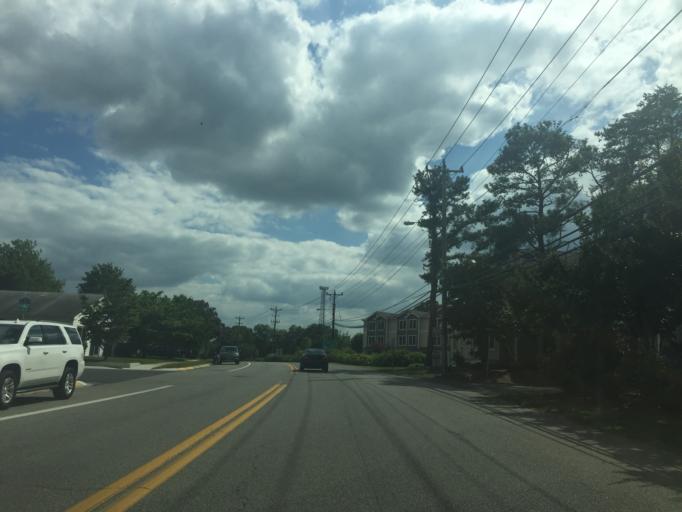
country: US
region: Delaware
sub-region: Sussex County
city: Rehoboth Beach
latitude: 38.7121
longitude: -75.0915
